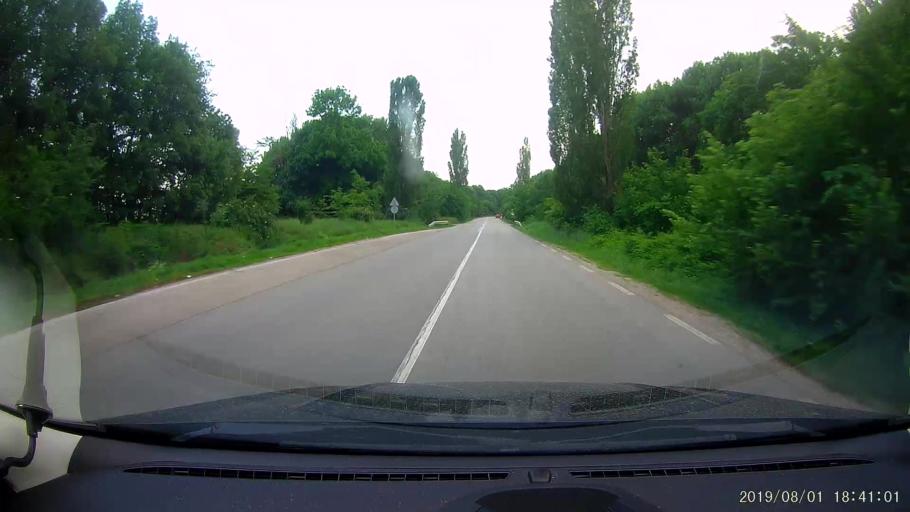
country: BG
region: Shumen
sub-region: Obshtina Khitrino
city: Gara Khitrino
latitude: 43.3536
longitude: 26.9228
